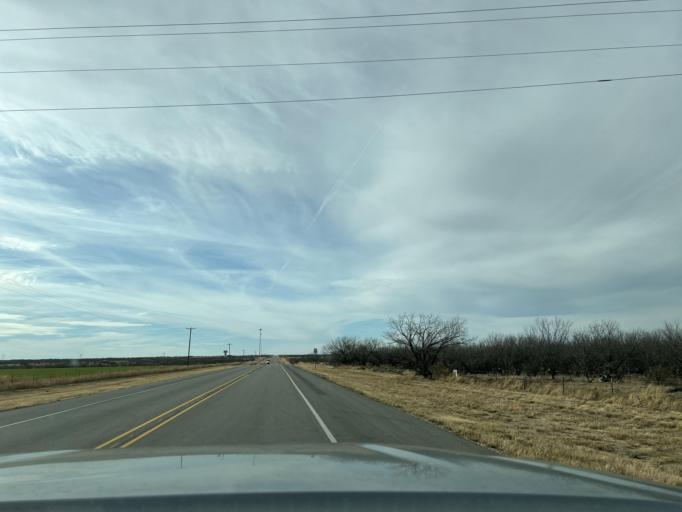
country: US
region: Texas
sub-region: Jones County
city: Anson
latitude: 32.7507
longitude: -99.7135
